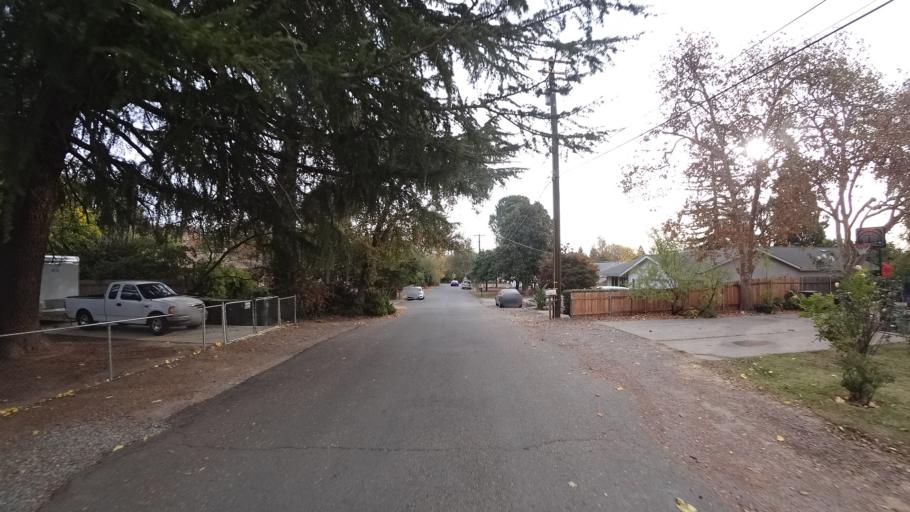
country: US
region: California
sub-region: Sacramento County
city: Citrus Heights
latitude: 38.7171
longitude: -121.2826
